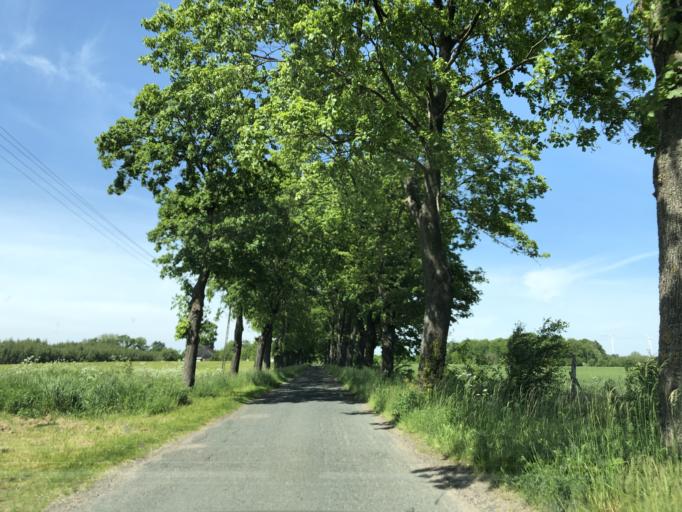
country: PL
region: West Pomeranian Voivodeship
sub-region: Powiat kolobrzeski
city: Goscino
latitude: 54.0400
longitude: 15.7286
